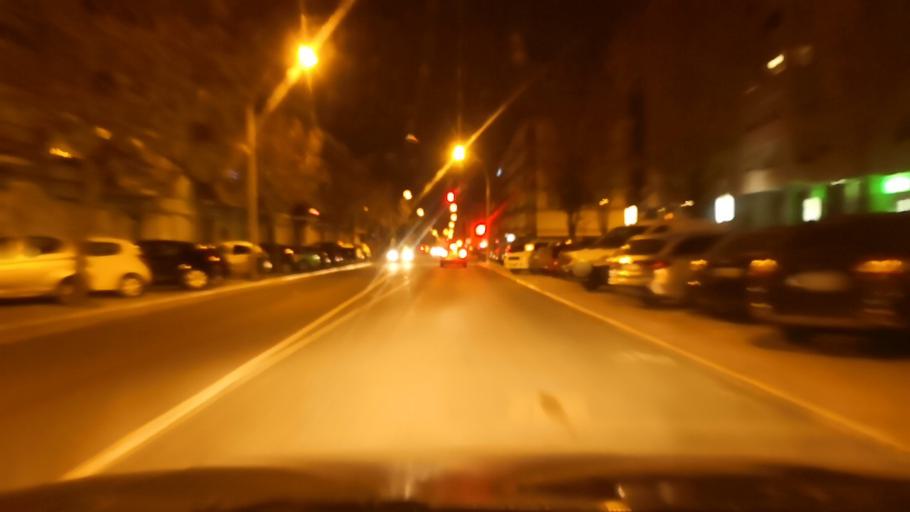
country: PT
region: Setubal
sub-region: Setubal
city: Setubal
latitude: 38.5380
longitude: -8.8945
